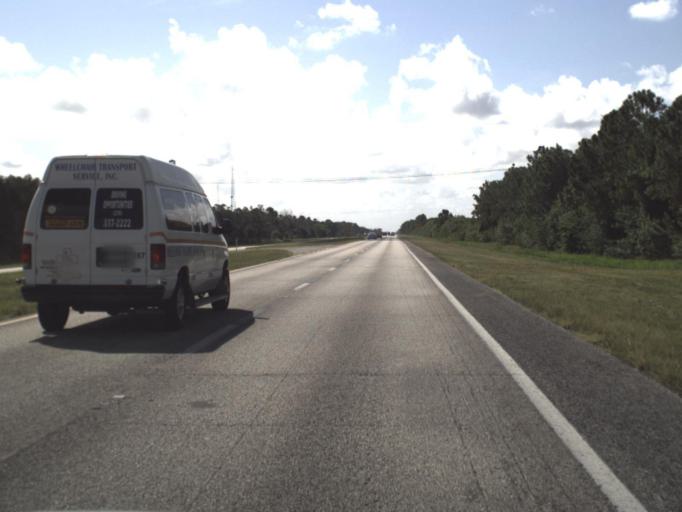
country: US
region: Florida
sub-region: Lee County
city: Burnt Store Marina
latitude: 26.8381
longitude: -81.9751
